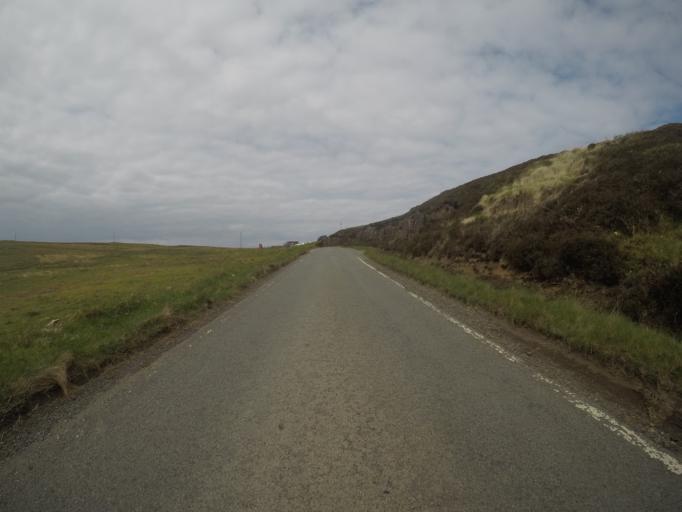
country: GB
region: Scotland
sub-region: Highland
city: Portree
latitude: 57.6834
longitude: -6.3256
